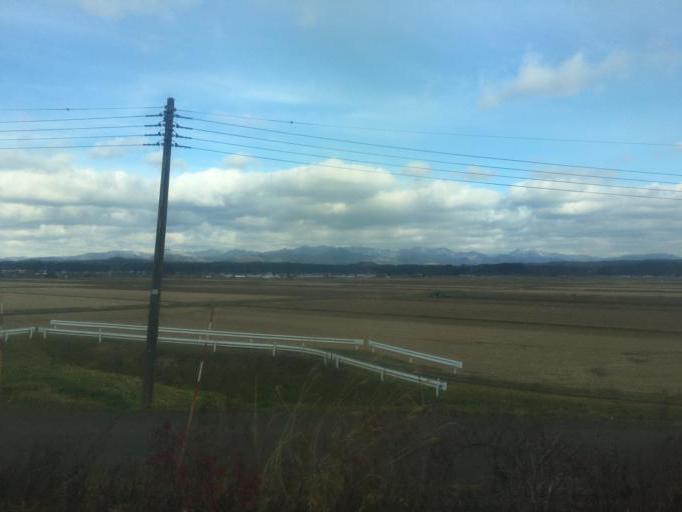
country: JP
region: Akita
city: Noshiromachi
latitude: 40.2121
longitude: 140.1466
